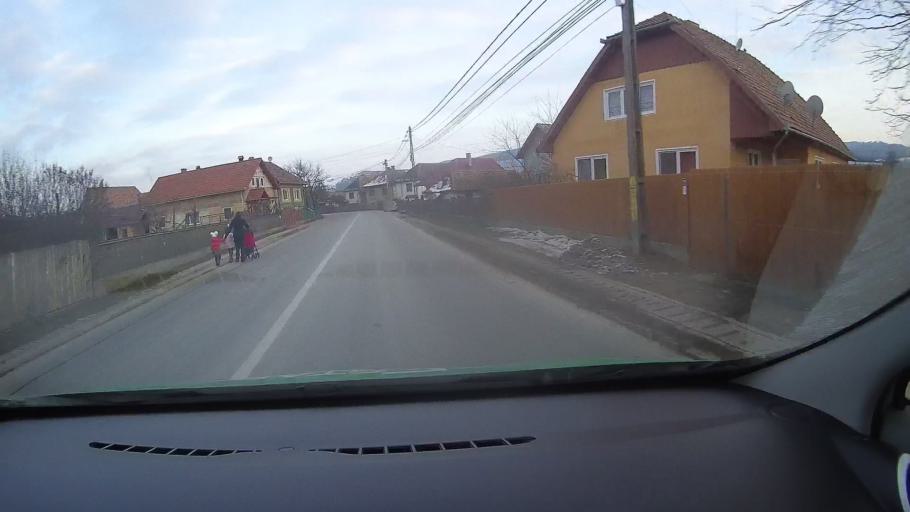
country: RO
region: Harghita
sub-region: Comuna Simonesti
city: Simonesti
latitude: 46.3570
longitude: 25.1445
